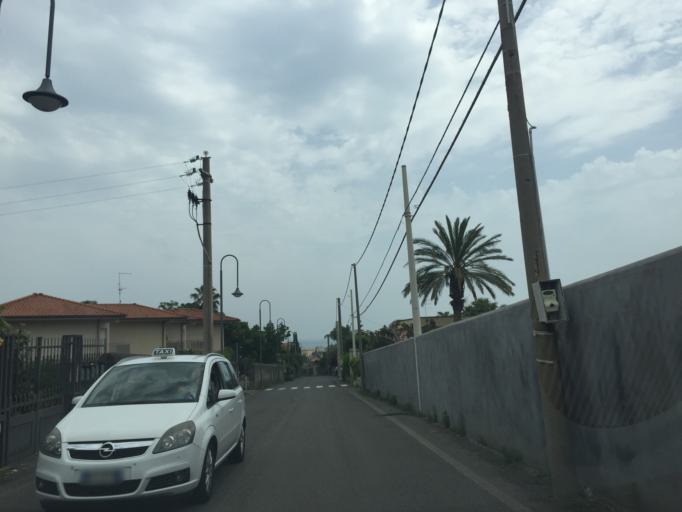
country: IT
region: Sicily
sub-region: Catania
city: Vambolieri
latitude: 37.5788
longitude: 15.1687
